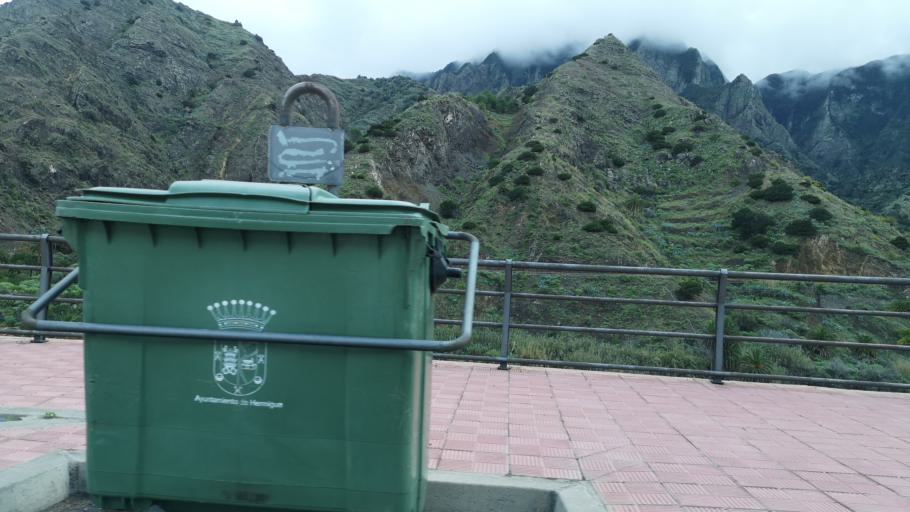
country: ES
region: Canary Islands
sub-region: Provincia de Santa Cruz de Tenerife
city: Hermigua
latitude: 28.1523
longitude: -17.1978
